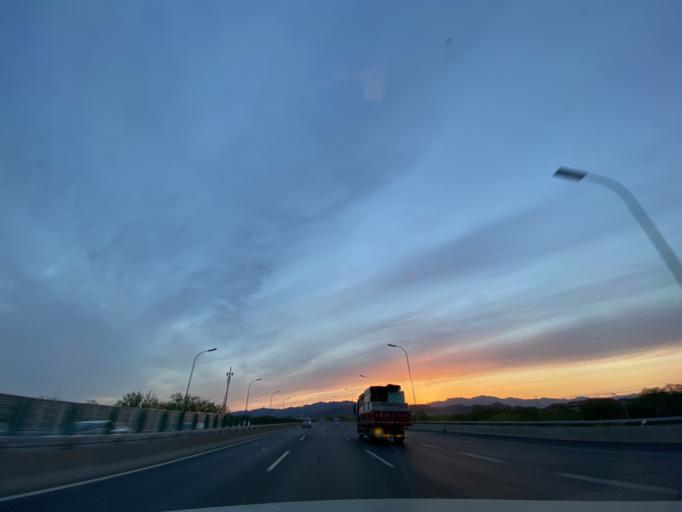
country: CN
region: Beijing
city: Qinghe
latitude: 40.0173
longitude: 116.3125
